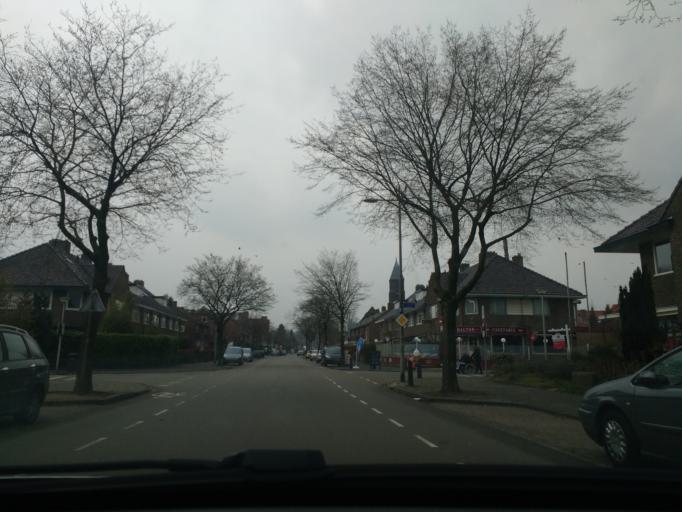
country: NL
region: Utrecht
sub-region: Gemeente Amersfoort
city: Amersfoort
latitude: 52.1439
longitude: 5.3846
